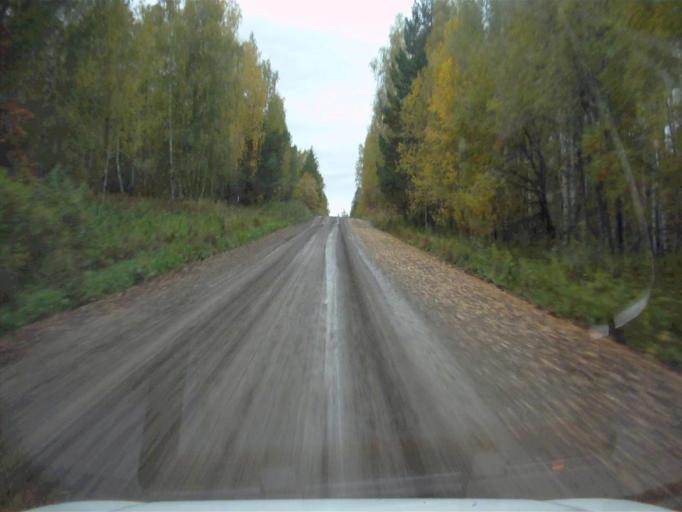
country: RU
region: Chelyabinsk
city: Nyazepetrovsk
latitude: 56.1055
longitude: 59.3838
